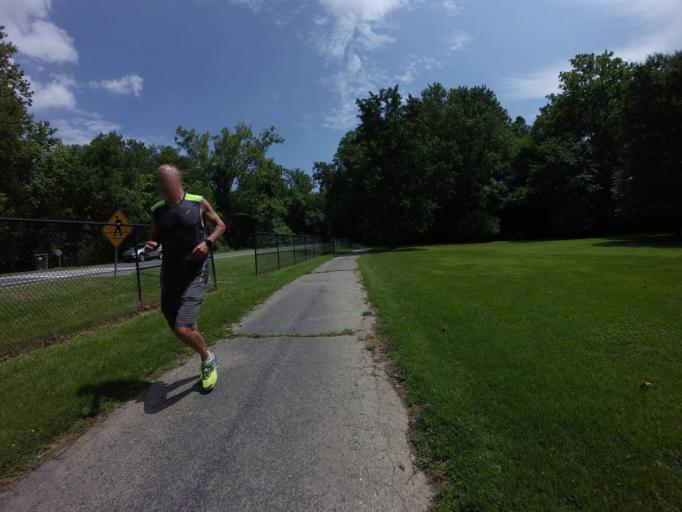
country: US
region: Maryland
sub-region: Montgomery County
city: South Kensington
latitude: 39.0277
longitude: -77.0894
